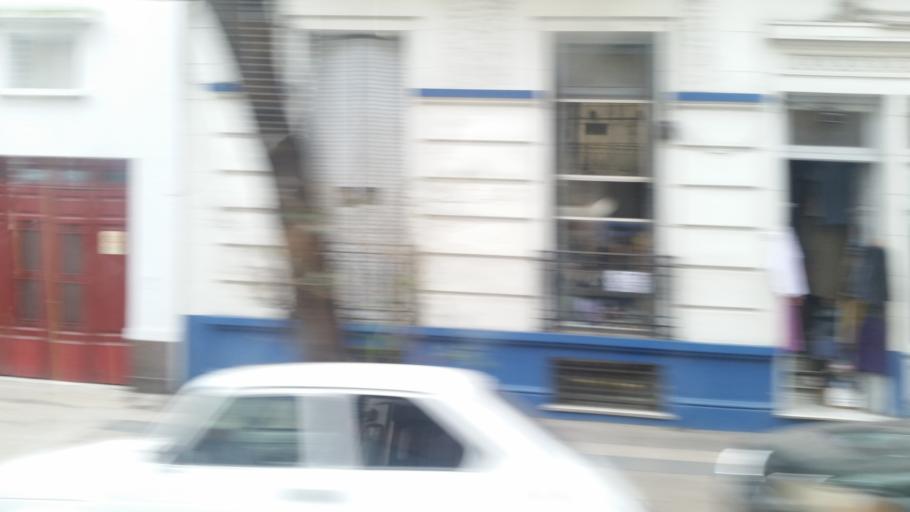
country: AR
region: Buenos Aires F.D.
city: Colegiales
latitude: -34.6072
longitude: -58.4217
